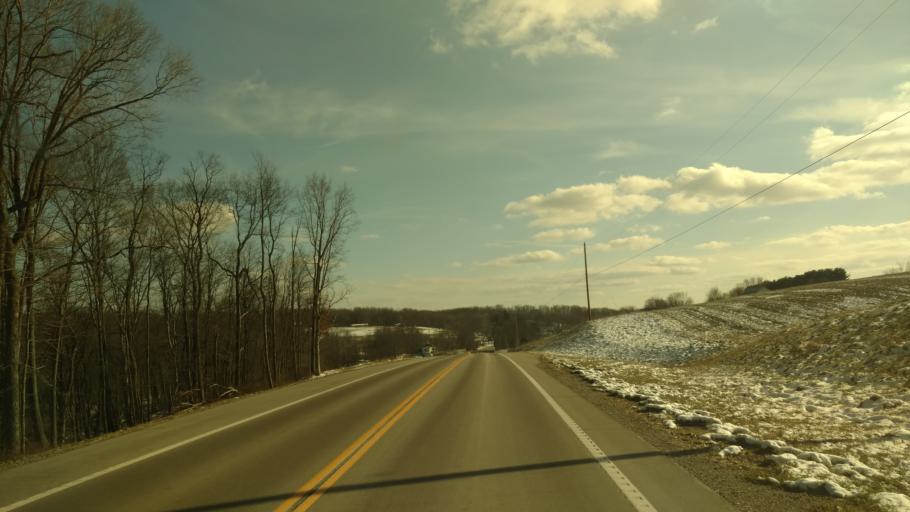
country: US
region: Ohio
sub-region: Ashland County
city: Loudonville
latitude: 40.7164
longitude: -82.2407
